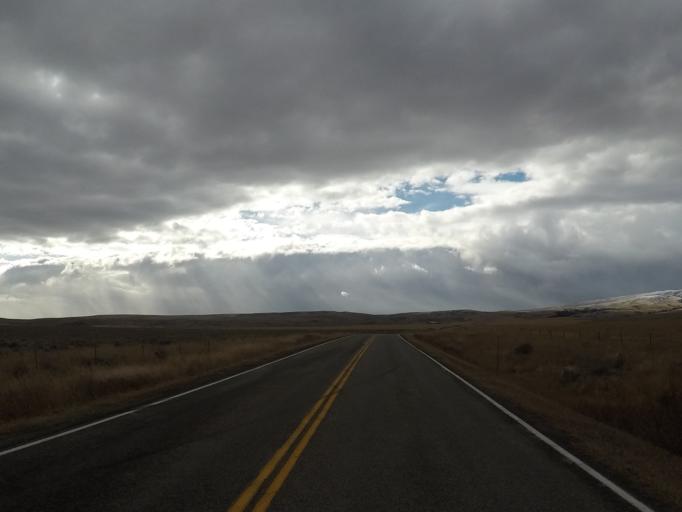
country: US
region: Montana
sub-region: Meagher County
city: White Sulphur Springs
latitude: 46.4111
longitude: -110.9244
